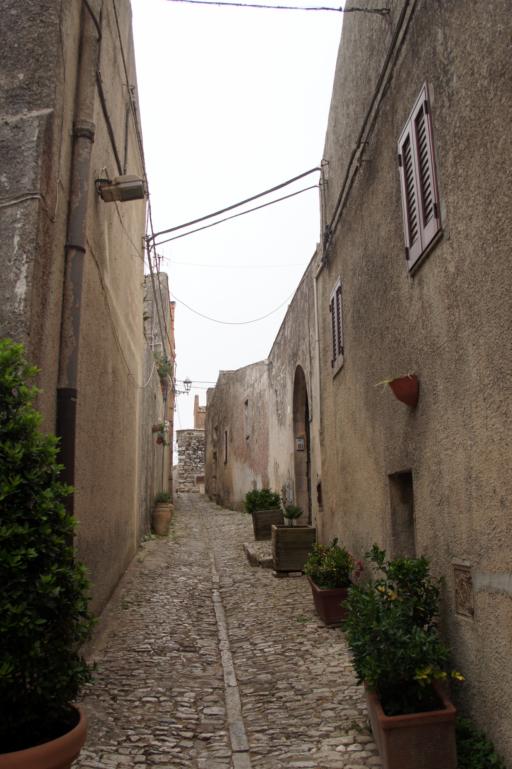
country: IT
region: Sicily
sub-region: Trapani
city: Erice
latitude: 38.0367
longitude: 12.5896
